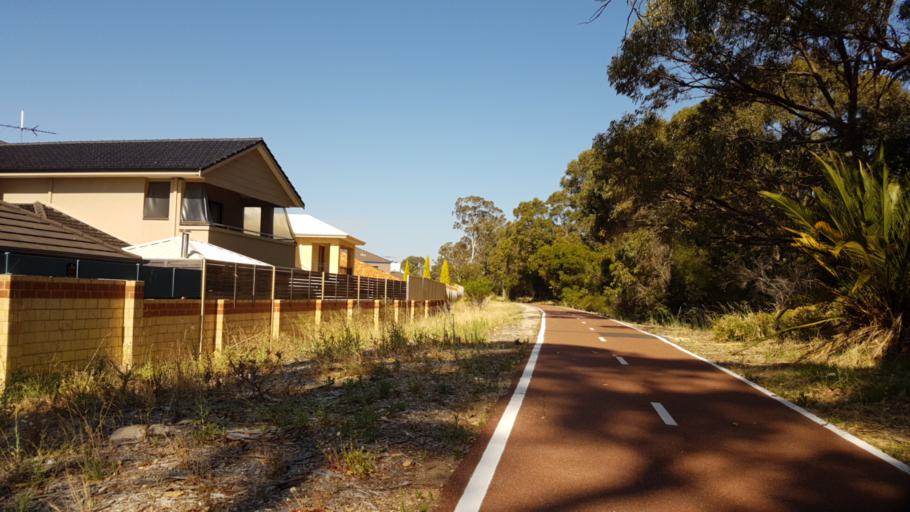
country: AU
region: Western Australia
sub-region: Stirling
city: Karrinyup
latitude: -31.8565
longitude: 115.7930
